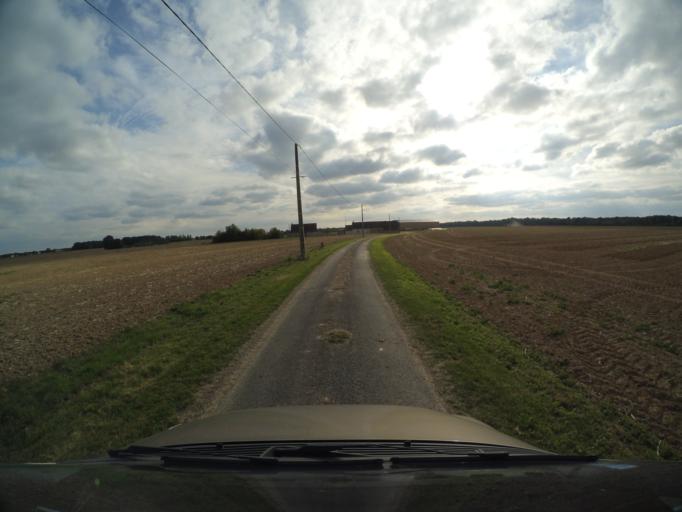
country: FR
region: Centre
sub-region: Departement d'Indre-et-Loire
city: Poce-sur-Cisse
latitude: 47.4676
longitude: 0.9670
